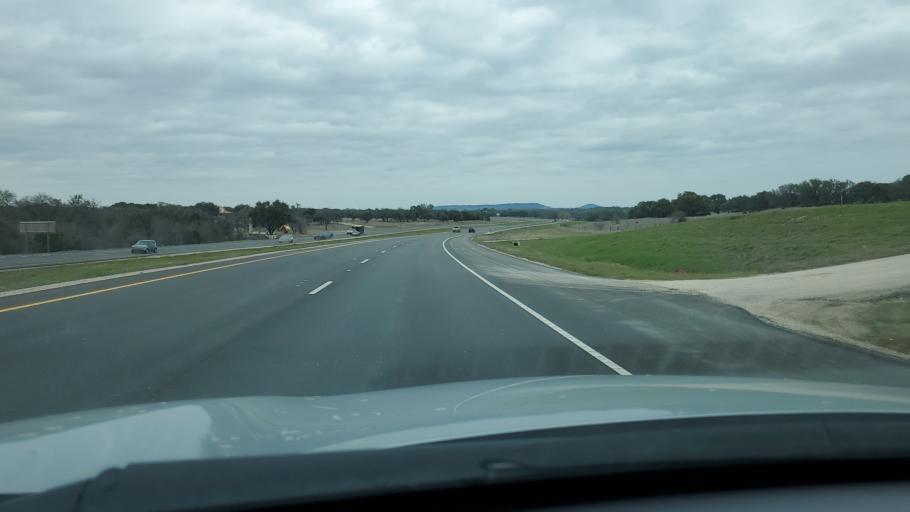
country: US
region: Texas
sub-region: Williamson County
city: Florence
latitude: 30.9360
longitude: -97.7909
